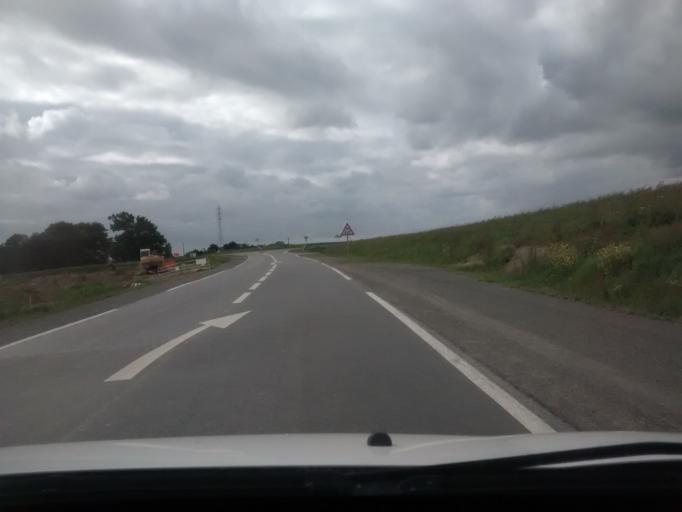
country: FR
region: Brittany
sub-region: Departement d'Ille-et-Vilaine
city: Noyal-sur-Vilaine
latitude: 48.0970
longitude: -1.5636
